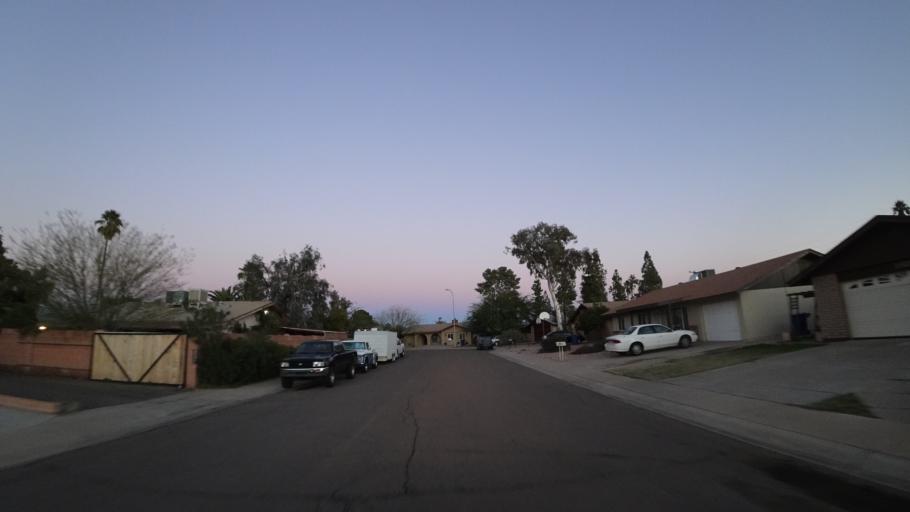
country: US
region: Arizona
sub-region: Maricopa County
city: Tempe Junction
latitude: 33.4139
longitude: -111.9593
